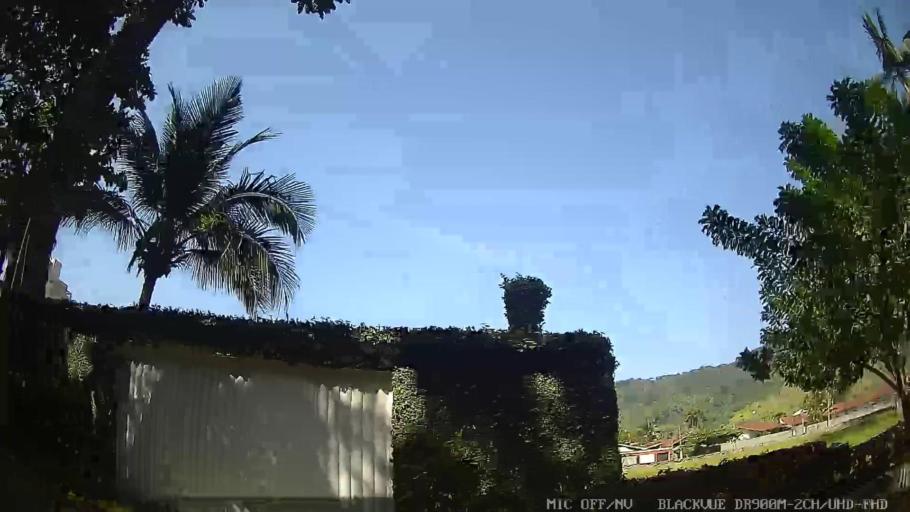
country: BR
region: Sao Paulo
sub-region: Guaruja
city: Guaruja
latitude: -24.0111
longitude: -46.2789
